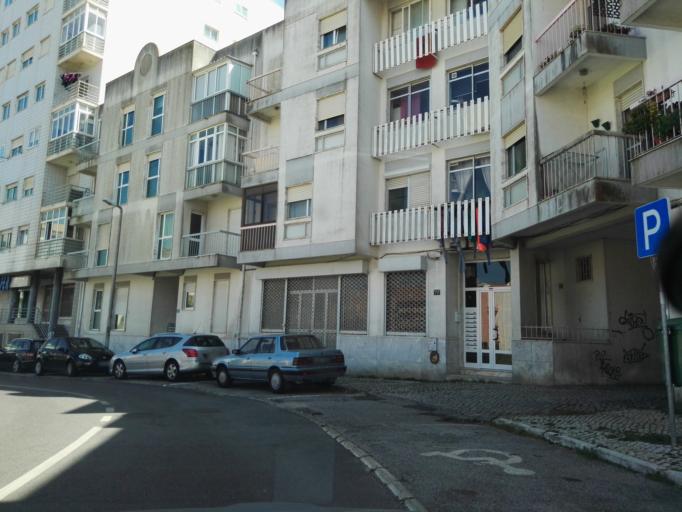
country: PT
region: Lisbon
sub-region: Sintra
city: Sintra
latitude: 38.7981
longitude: -9.3558
